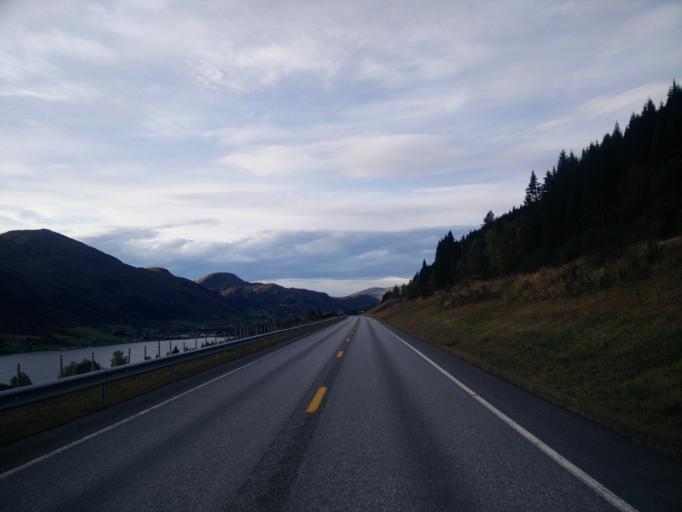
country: NO
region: More og Romsdal
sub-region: Gjemnes
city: Batnfjordsora
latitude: 62.9170
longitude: 7.6938
